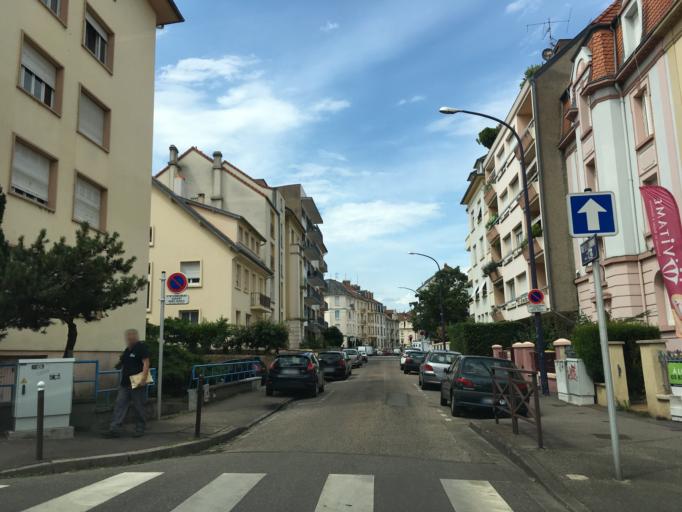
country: FR
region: Lorraine
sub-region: Departement de la Moselle
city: Metz
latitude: 49.1015
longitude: 6.1739
